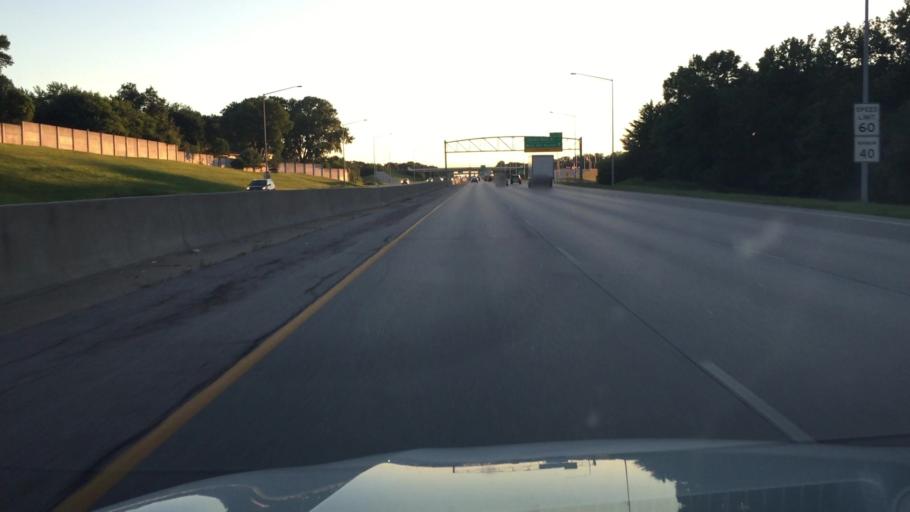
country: US
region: Iowa
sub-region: Polk County
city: Clive
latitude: 41.5924
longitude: -93.7440
